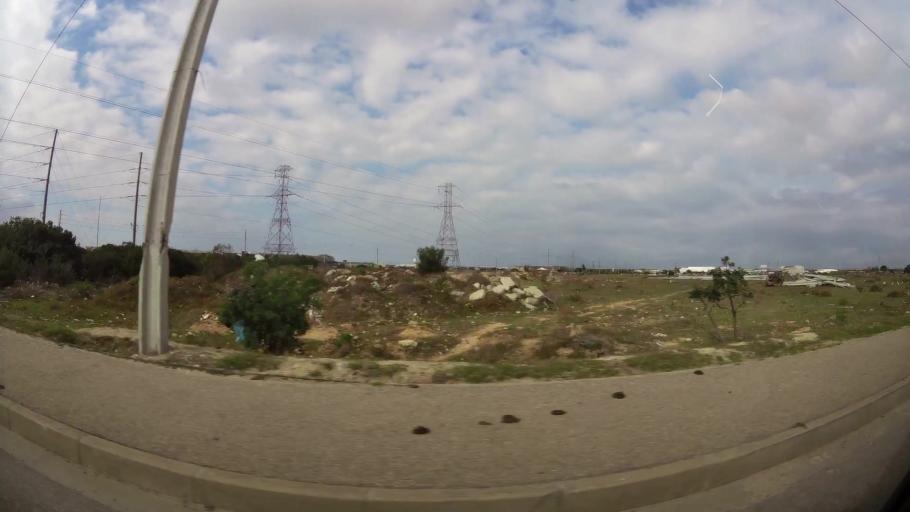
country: ZA
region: Eastern Cape
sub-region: Nelson Mandela Bay Metropolitan Municipality
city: Port Elizabeth
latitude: -33.8043
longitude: 25.6203
